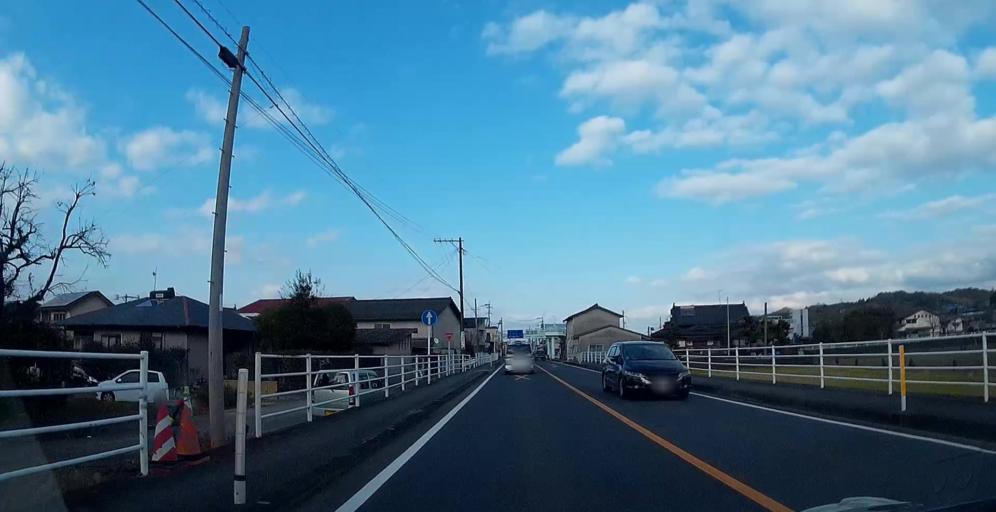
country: JP
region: Kumamoto
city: Yatsushiro
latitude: 32.5525
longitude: 130.6795
